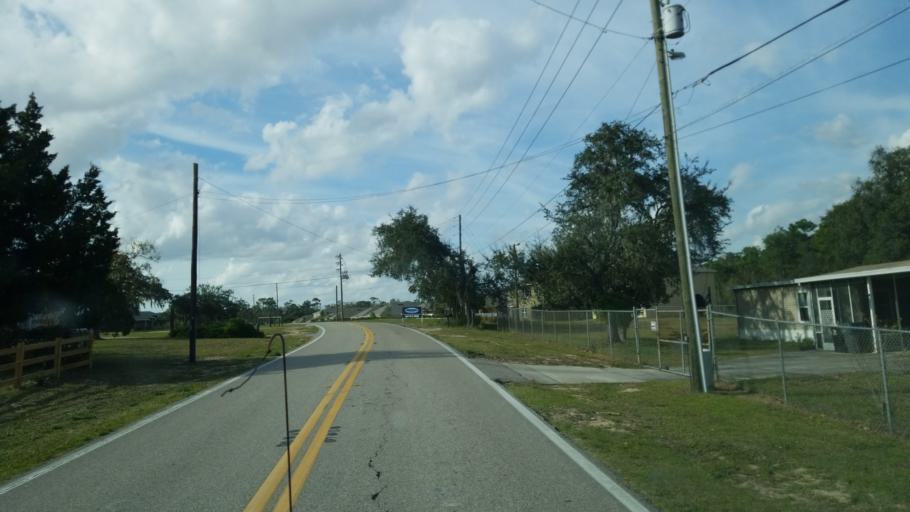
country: US
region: Florida
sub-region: Polk County
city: Loughman
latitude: 28.2518
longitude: -81.5702
